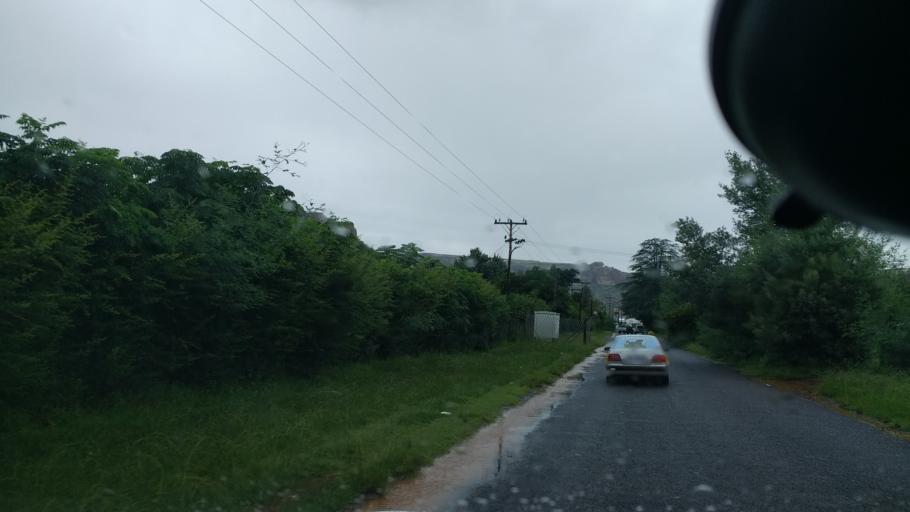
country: LS
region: Maseru
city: Nako
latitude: -29.4589
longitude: 27.7332
